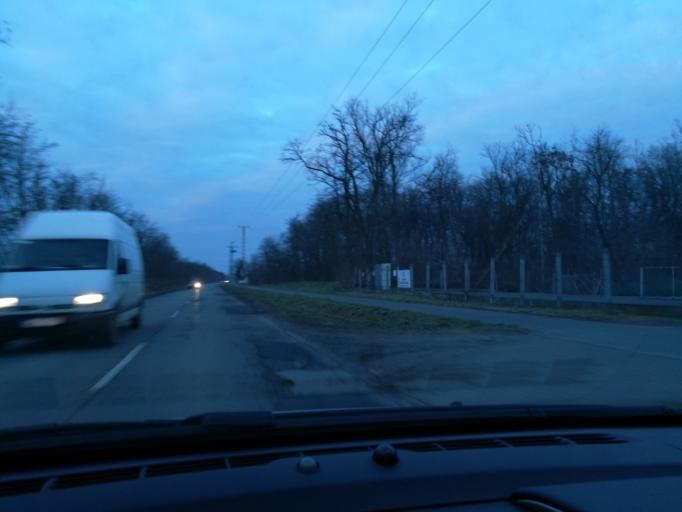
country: HU
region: Szabolcs-Szatmar-Bereg
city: Nyiregyhaza
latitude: 47.9813
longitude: 21.7047
